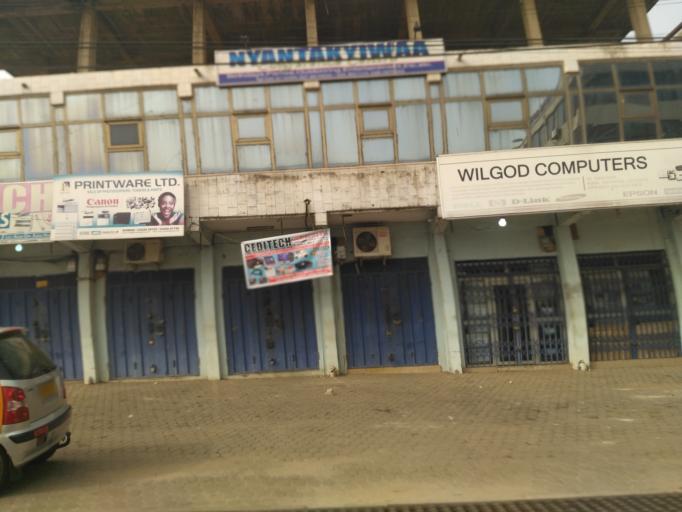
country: GH
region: Ashanti
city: Kumasi
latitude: 6.6886
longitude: -1.6197
